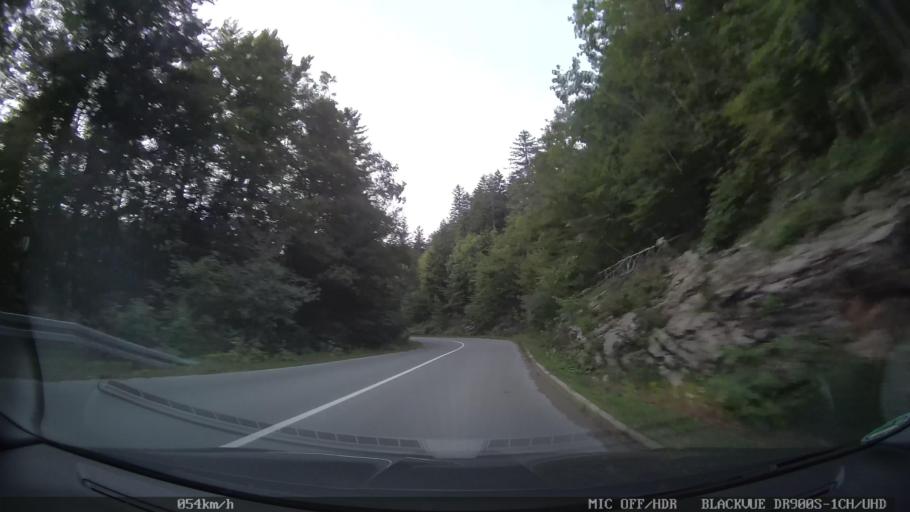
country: HR
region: Primorsko-Goranska
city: Novi Vinodolski
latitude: 45.1645
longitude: 14.9473
